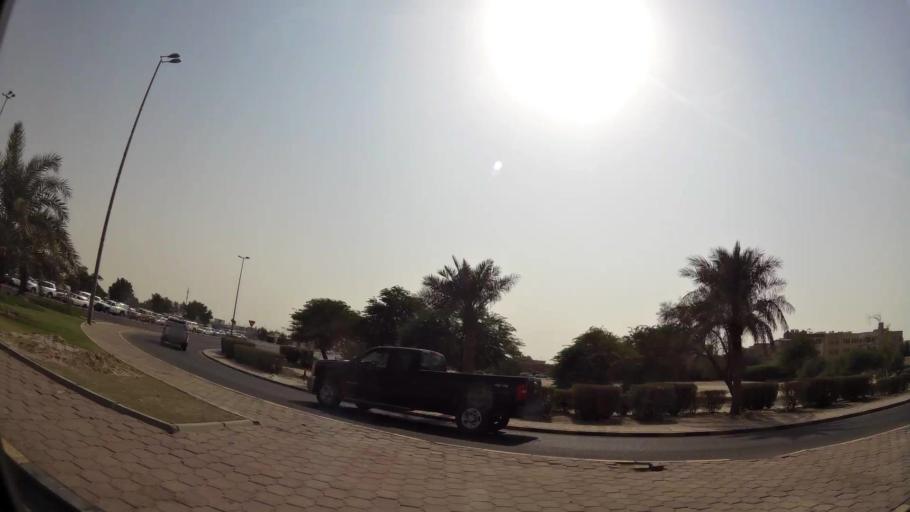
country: KW
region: Muhafazat al Jahra'
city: Al Jahra'
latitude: 29.3359
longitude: 47.6657
